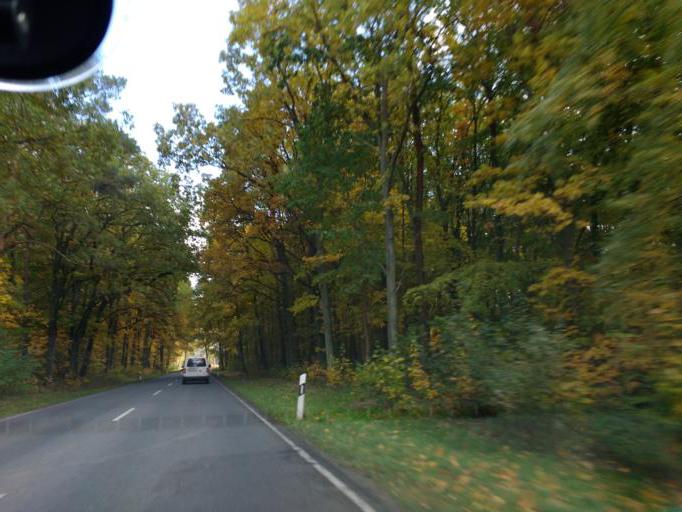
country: DE
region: Brandenburg
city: Petershagen
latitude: 52.5578
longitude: 13.7872
